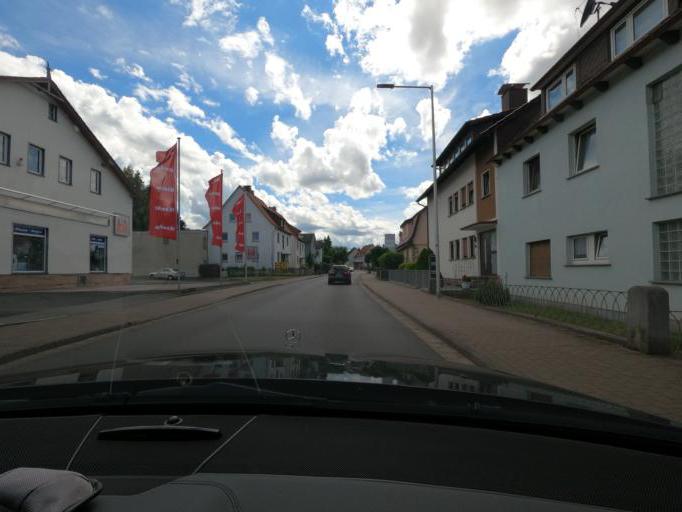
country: DE
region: Hesse
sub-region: Regierungsbezirk Kassel
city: Sontra
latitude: 51.0746
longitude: 9.9372
